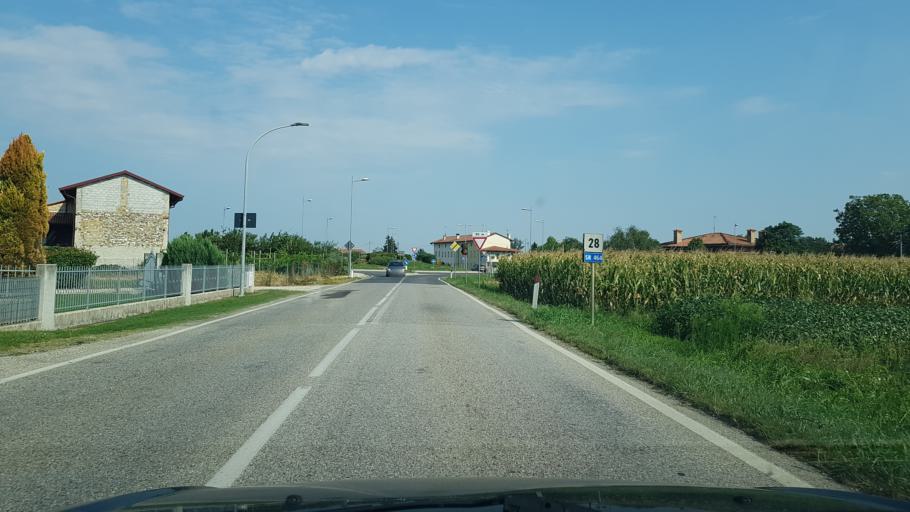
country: IT
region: Friuli Venezia Giulia
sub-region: Provincia di Udine
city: Flaibano
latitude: 46.0820
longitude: 12.9876
